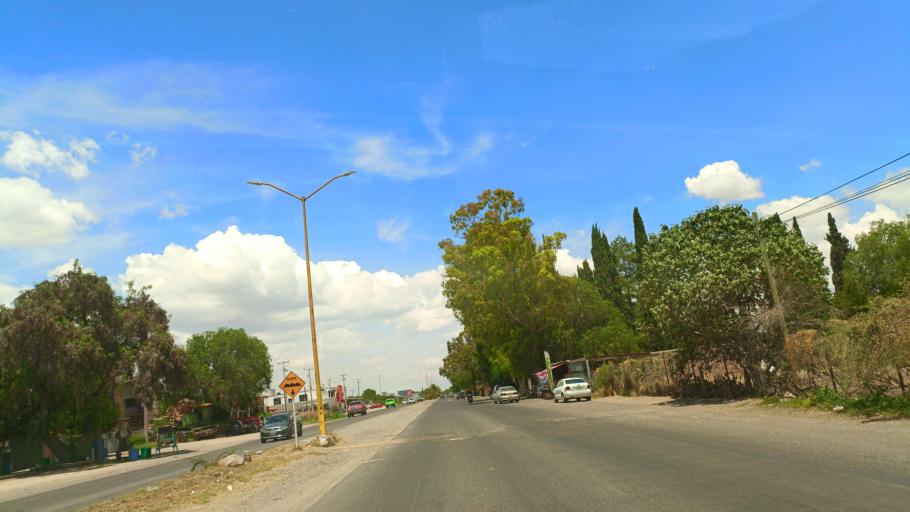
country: MX
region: Guanajuato
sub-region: San Luis de la Paz
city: San Ignacio
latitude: 21.2905
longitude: -100.5471
